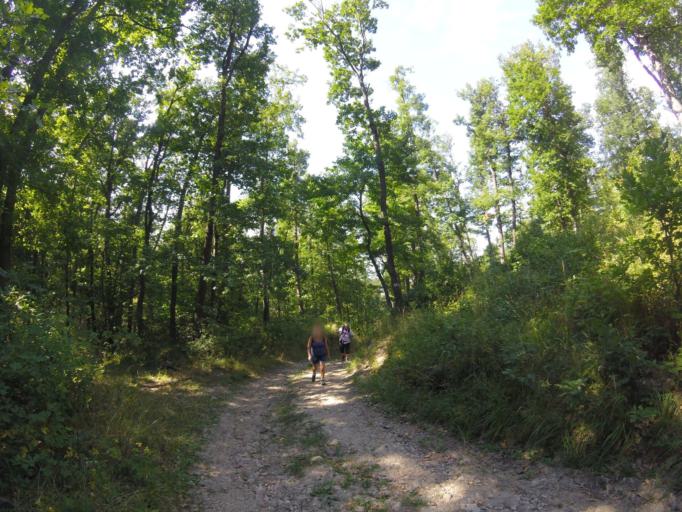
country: HU
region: Pest
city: Csobanka
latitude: 47.6806
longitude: 18.9788
